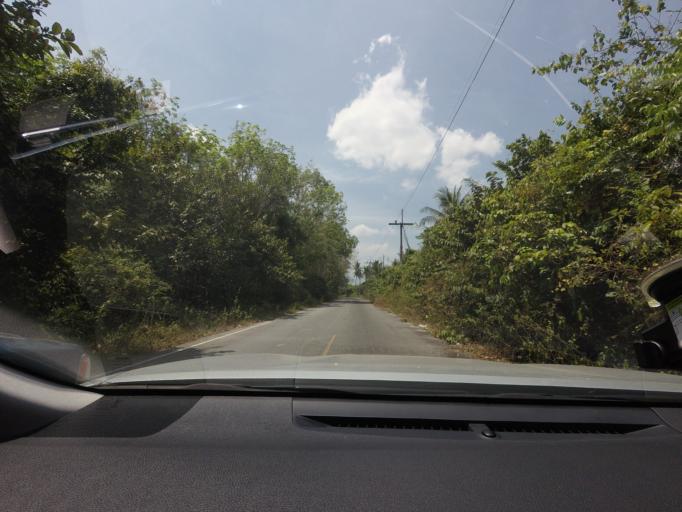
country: TH
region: Narathiwat
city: Rueso
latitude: 6.3849
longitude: 101.5086
